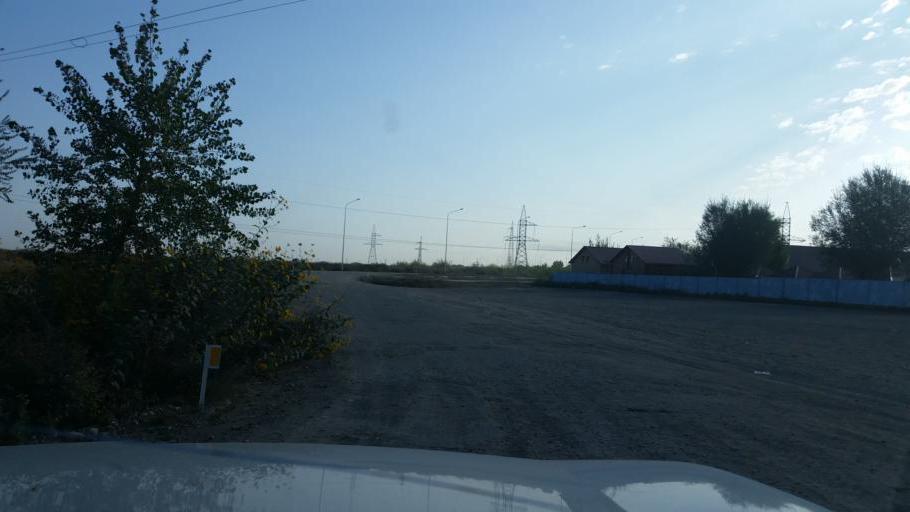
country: KZ
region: Almaty Oblysy
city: Energeticheskiy
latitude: 43.4428
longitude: 76.9892
